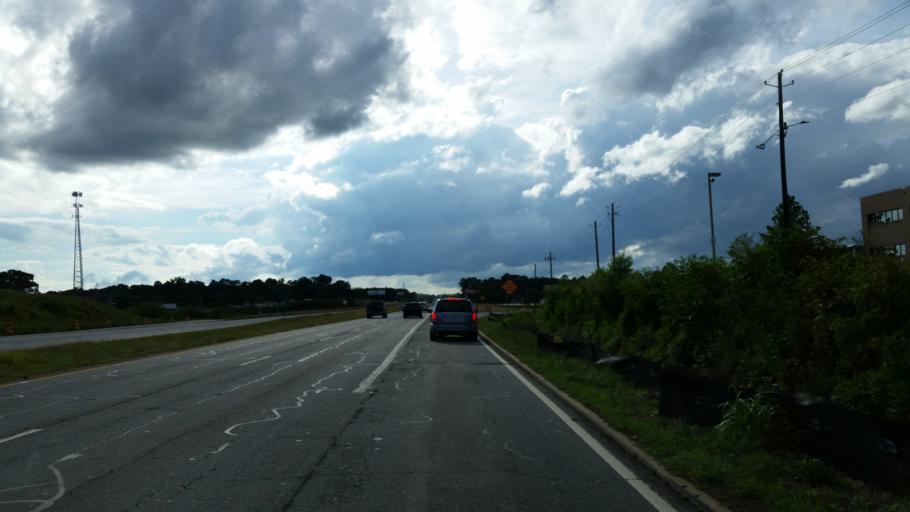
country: US
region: Georgia
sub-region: Bartow County
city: Cartersville
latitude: 34.1999
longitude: -84.7957
